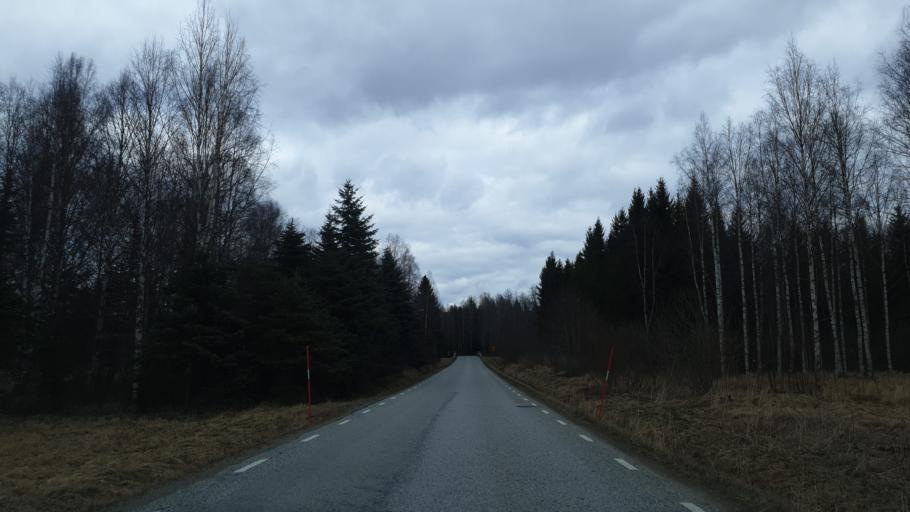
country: SE
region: OErebro
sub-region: Nora Kommun
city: As
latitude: 59.6286
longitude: 14.9350
